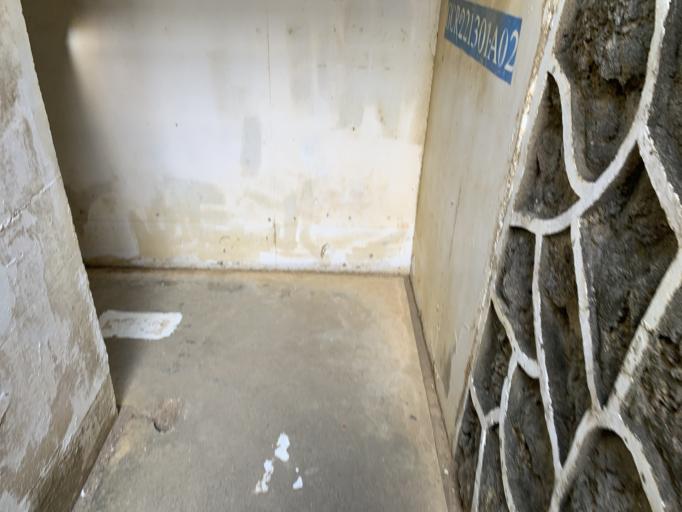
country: TW
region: Kaohsiung
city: Kaohsiung
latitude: 22.3443
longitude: 120.3623
